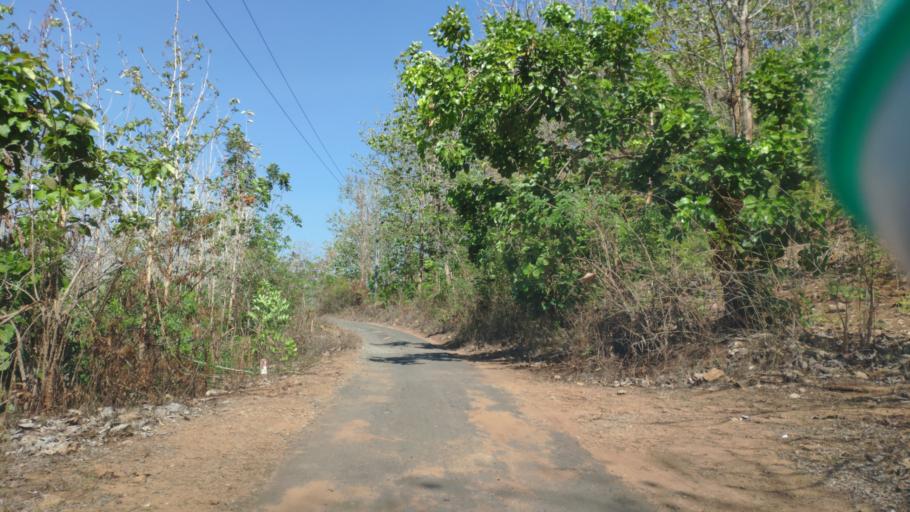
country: ID
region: East Java
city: Krajan Jamprong
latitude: -6.9906
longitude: 111.6156
